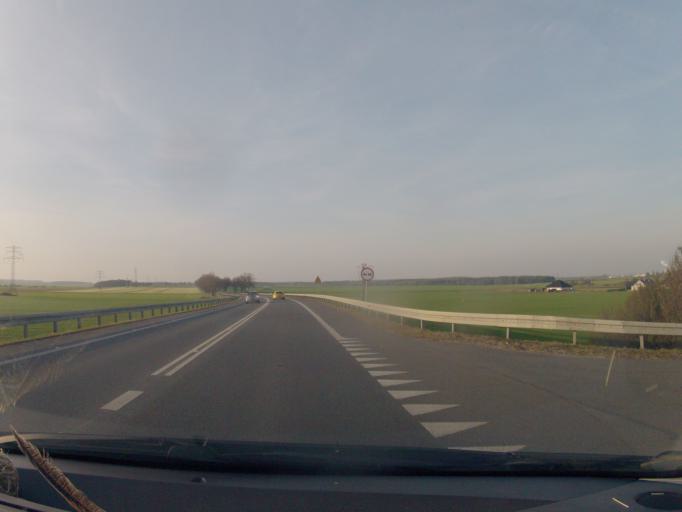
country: PL
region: Opole Voivodeship
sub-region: Powiat strzelecki
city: Strzelce Opolskie
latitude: 50.5231
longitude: 18.2773
